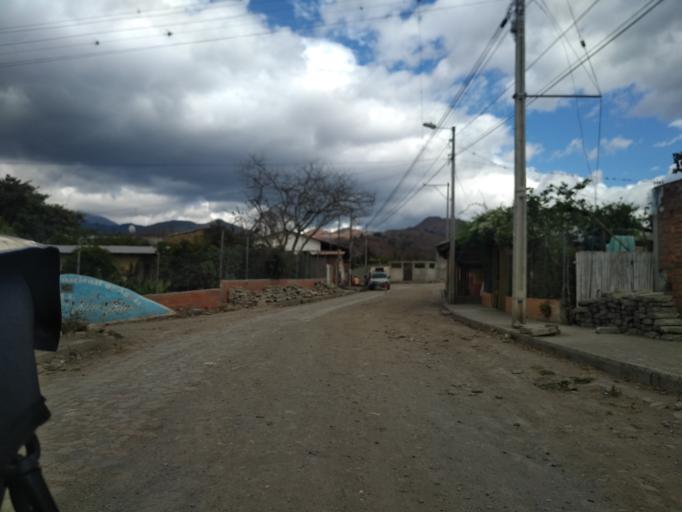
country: EC
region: Loja
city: Loja
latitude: -4.2567
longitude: -79.2218
